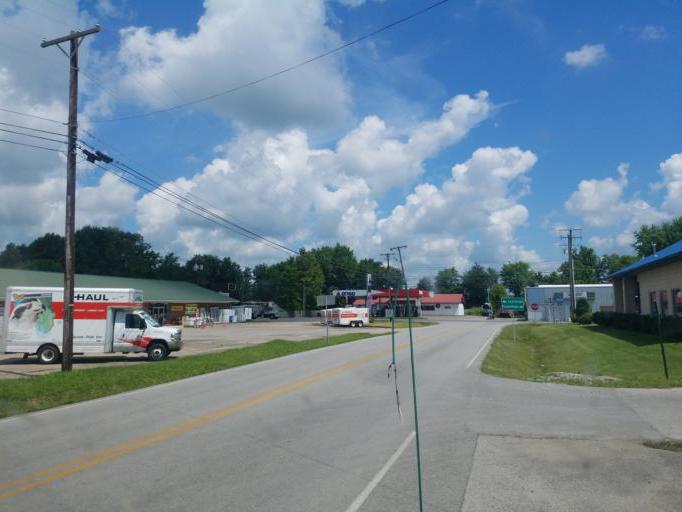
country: US
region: Kentucky
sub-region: Grayson County
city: Leitchfield
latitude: 37.4947
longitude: -86.2254
